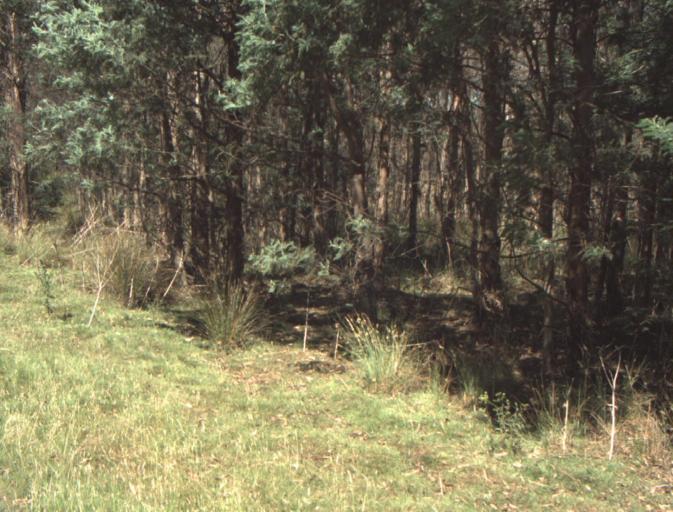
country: AU
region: Tasmania
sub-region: Dorset
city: Scottsdale
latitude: -41.2682
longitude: 147.3519
